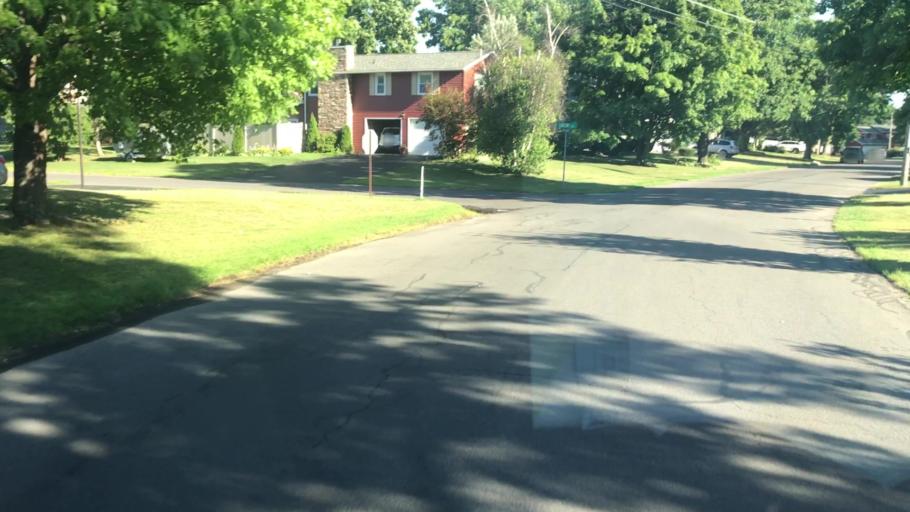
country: US
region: New York
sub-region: Onondaga County
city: Liverpool
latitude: 43.1353
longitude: -76.2163
